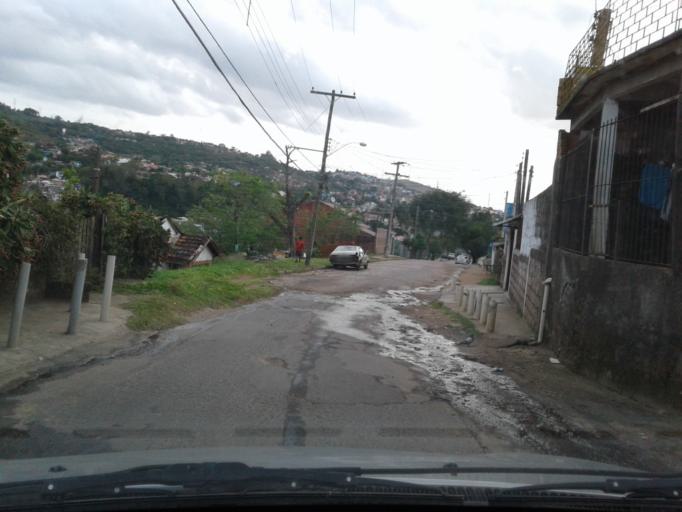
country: BR
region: Rio Grande do Sul
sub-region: Porto Alegre
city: Porto Alegre
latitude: -30.0640
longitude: -51.1460
